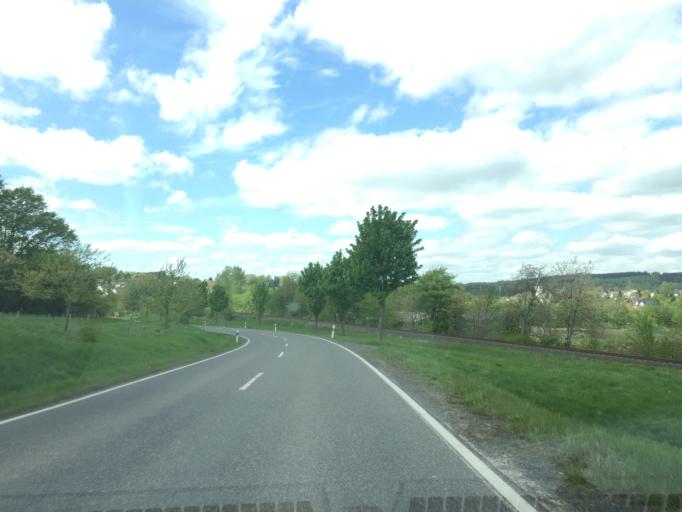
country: DE
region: Rheinland-Pfalz
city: Meudt
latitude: 50.4898
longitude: 7.9046
